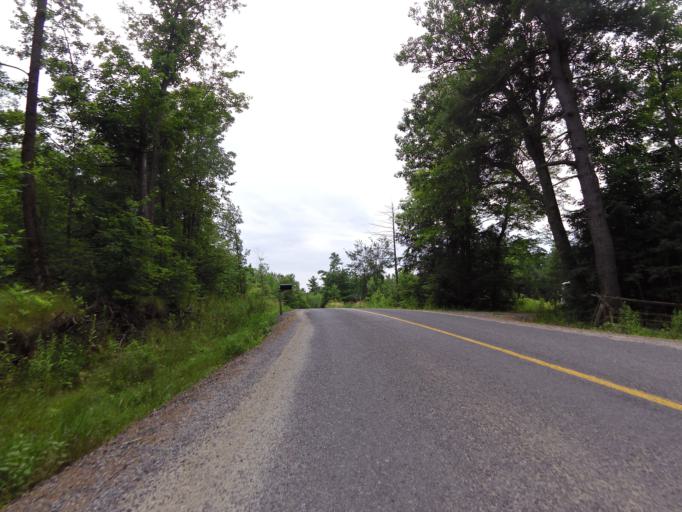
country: CA
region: Ontario
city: Kingston
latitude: 44.6639
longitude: -76.6581
